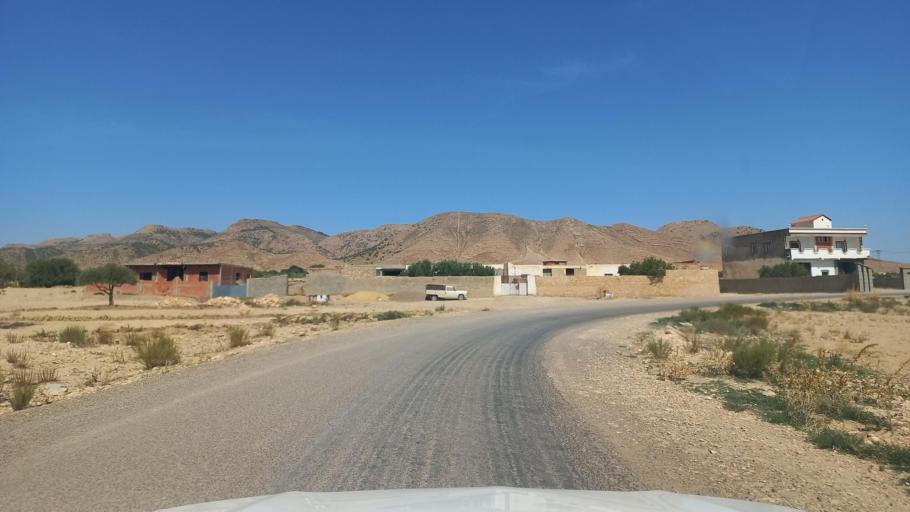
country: TN
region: Al Qasrayn
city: Sbiba
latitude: 35.4416
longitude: 9.0737
